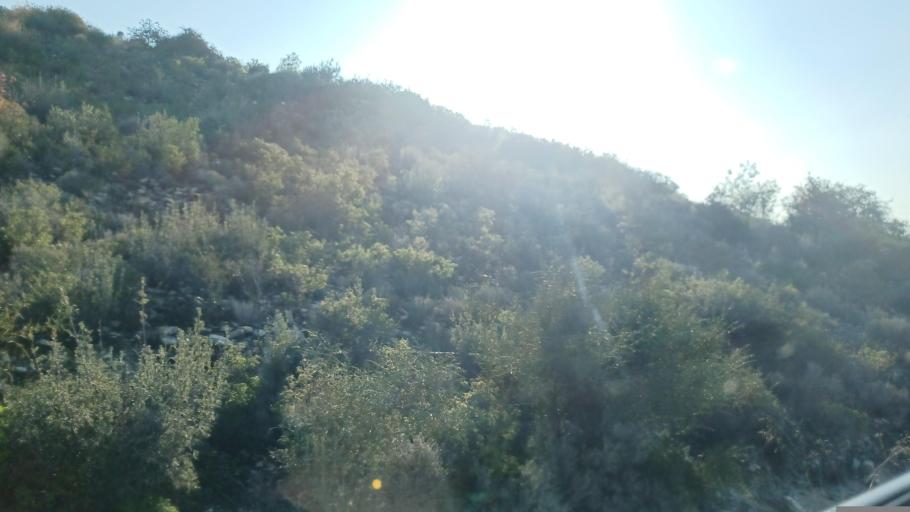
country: CY
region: Larnaka
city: Kofinou
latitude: 34.8299
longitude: 33.3039
